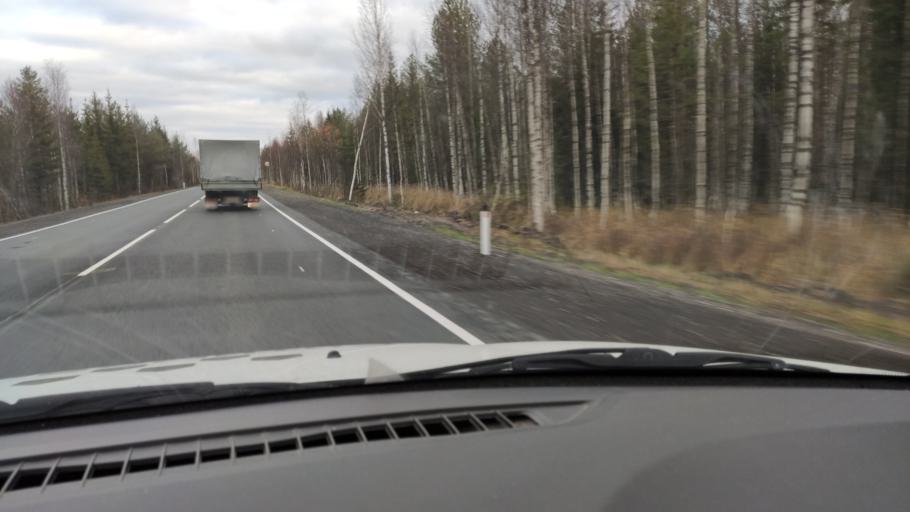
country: RU
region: Kirov
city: Chernaya Kholunitsa
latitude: 58.8740
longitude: 51.5009
